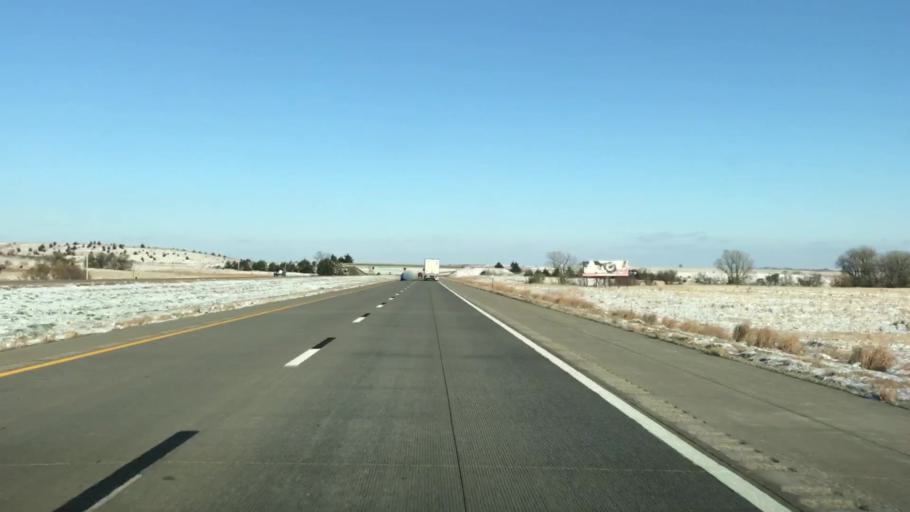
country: US
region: Kansas
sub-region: Lincoln County
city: Lincoln
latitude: 38.8755
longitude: -98.0275
